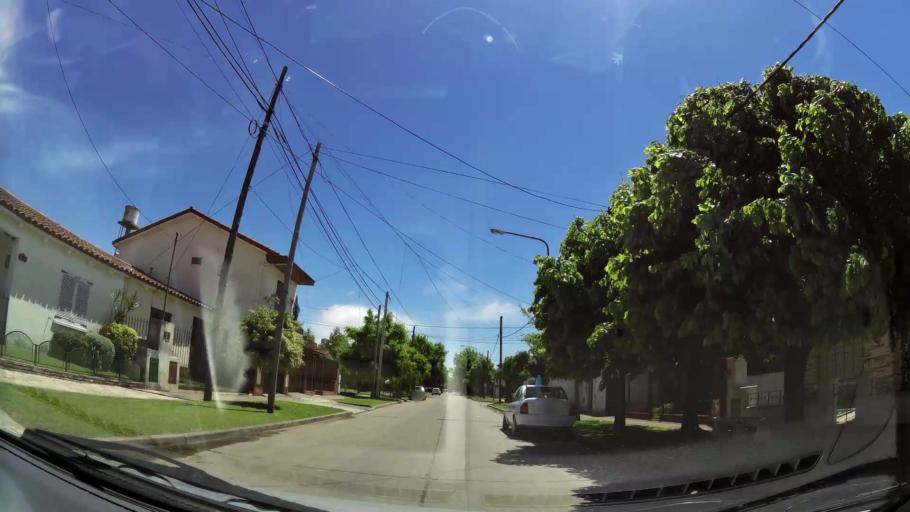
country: AR
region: Buenos Aires
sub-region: Partido de Quilmes
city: Quilmes
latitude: -34.7405
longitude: -58.2775
